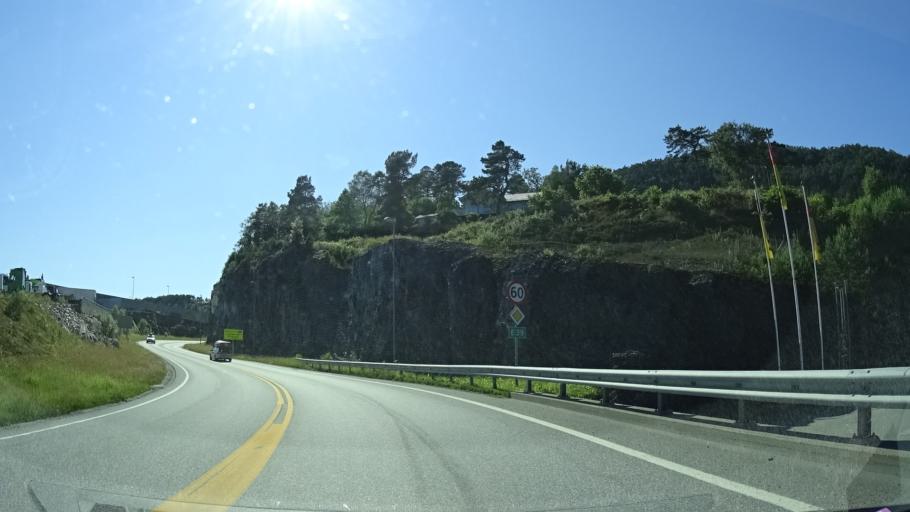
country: NO
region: Hordaland
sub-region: Os
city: Osoyro
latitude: 60.2057
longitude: 5.4490
